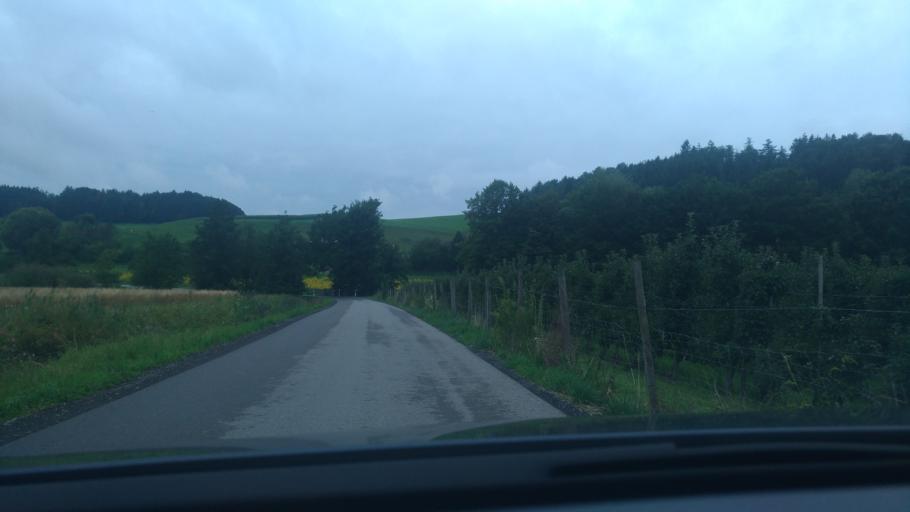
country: DE
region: Baden-Wuerttemberg
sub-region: Freiburg Region
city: Bodman-Ludwigshafen
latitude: 47.8571
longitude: 9.1008
